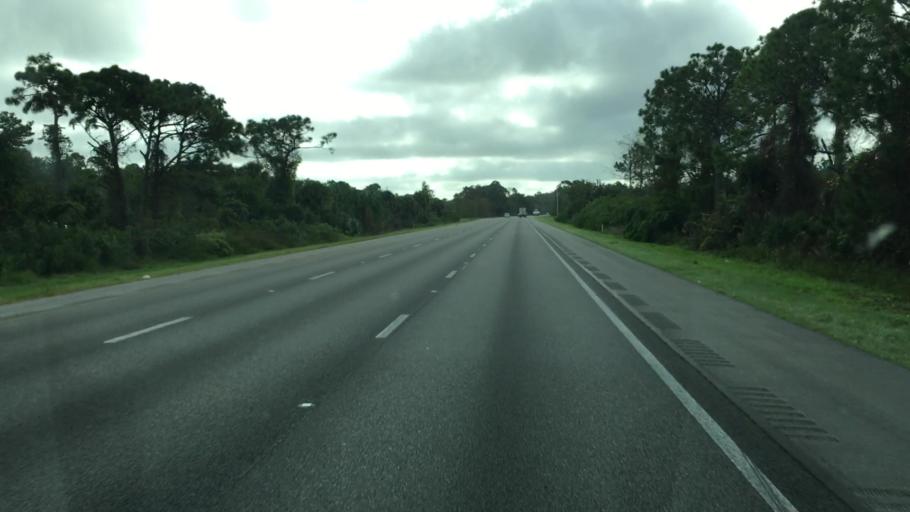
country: US
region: Florida
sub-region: Volusia County
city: Samsula-Spruce Creek
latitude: 29.0723
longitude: -81.0124
